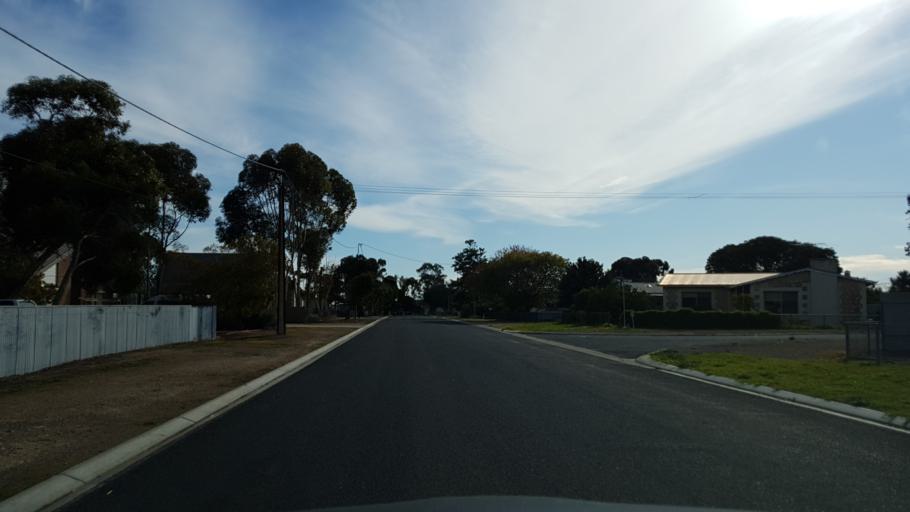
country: AU
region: South Australia
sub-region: Murray Bridge
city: Tailem Bend
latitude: -35.2523
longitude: 139.4627
